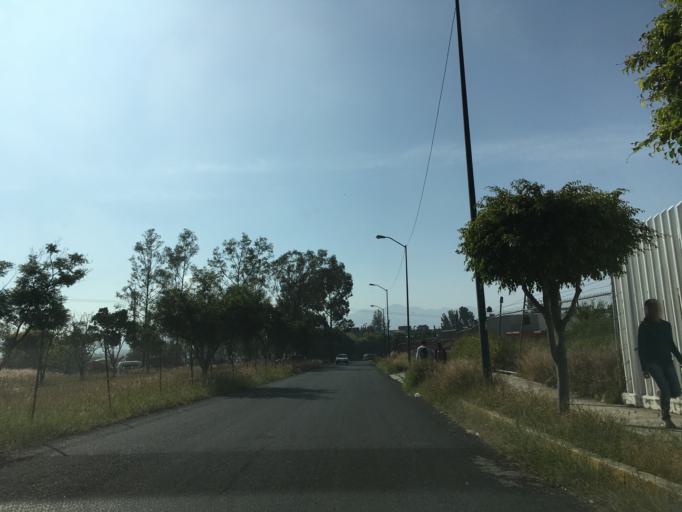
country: MX
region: Michoacan
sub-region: Tarimbaro
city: Fraccionamiento Metropolis II
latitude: 19.7157
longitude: -101.2321
